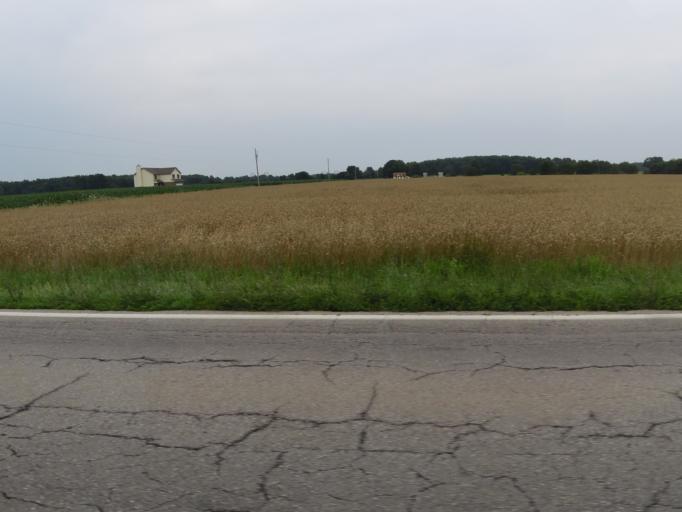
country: US
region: Ohio
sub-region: Clinton County
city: Blanchester
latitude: 39.2608
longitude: -83.9031
